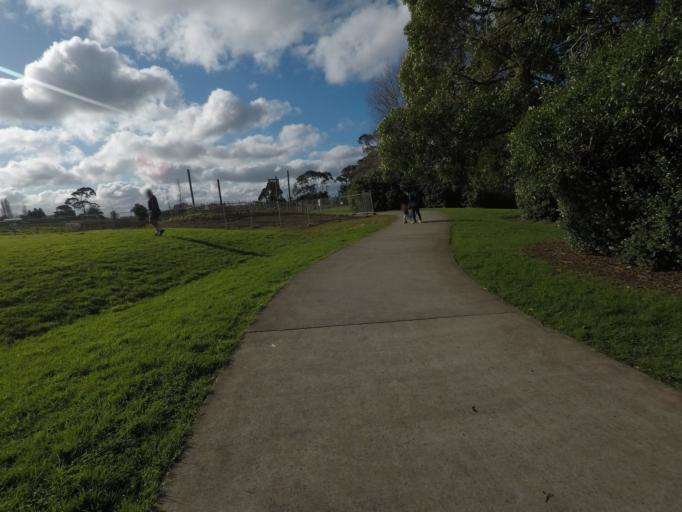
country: NZ
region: Auckland
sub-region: Auckland
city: Rosebank
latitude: -36.8946
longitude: 174.6714
